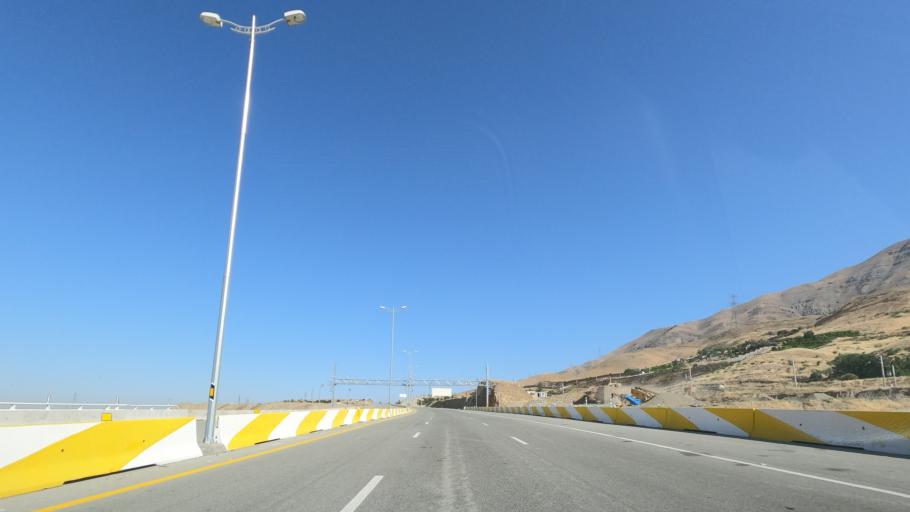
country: IR
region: Tehran
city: Shahr-e Qods
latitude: 35.7612
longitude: 51.0748
